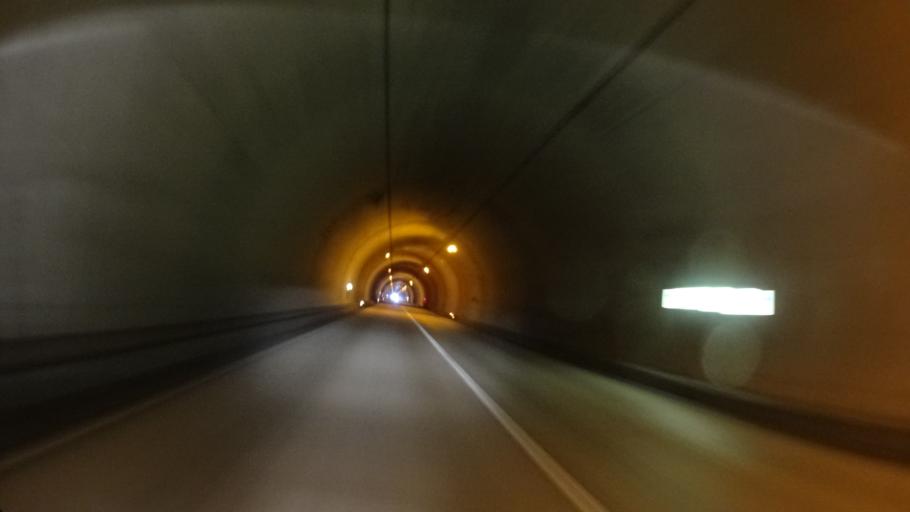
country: JP
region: Fukui
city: Maruoka
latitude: 36.1808
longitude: 136.3404
